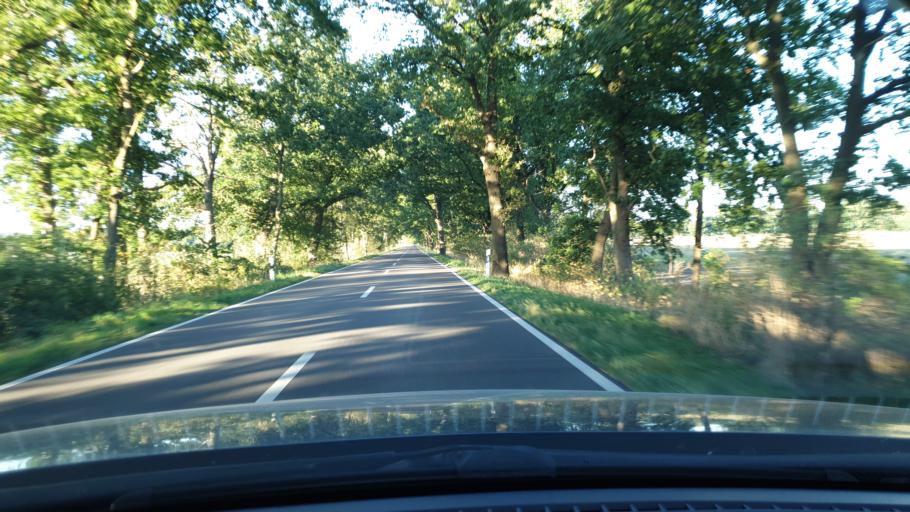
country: DE
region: Mecklenburg-Vorpommern
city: Lubtheen
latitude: 53.3479
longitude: 10.9580
